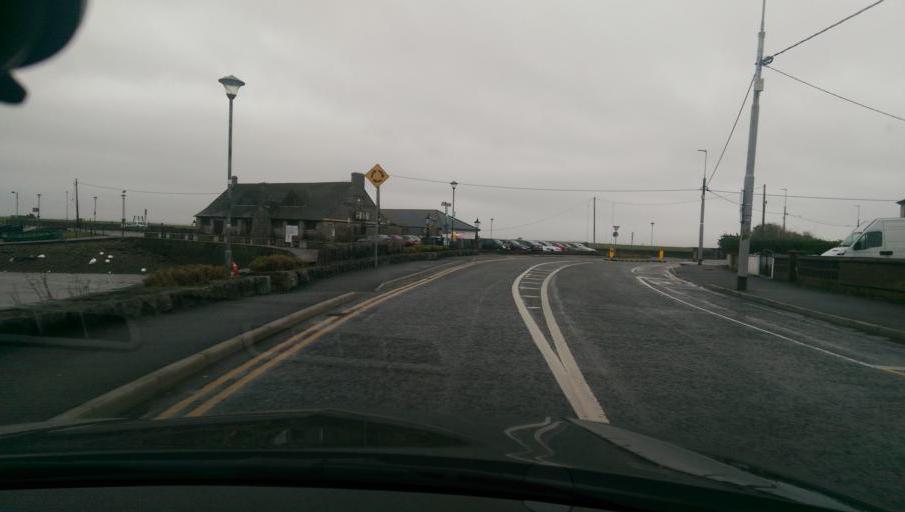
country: IE
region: Connaught
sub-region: County Galway
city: Gaillimh
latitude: 53.2678
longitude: -9.0547
